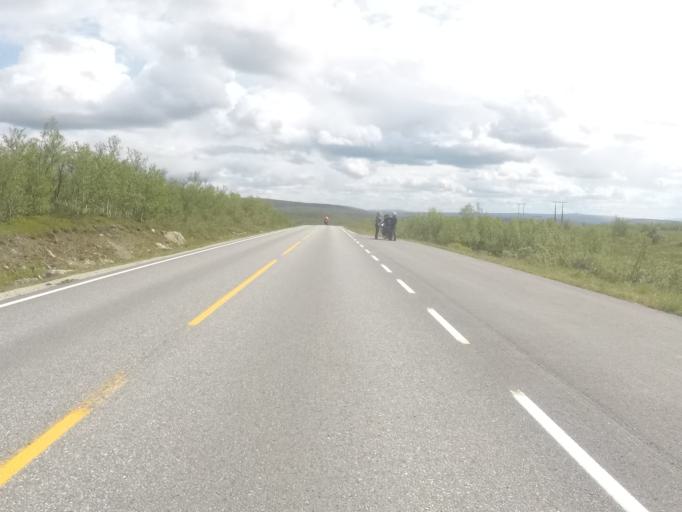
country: NO
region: Finnmark Fylke
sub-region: Karasjok
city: Karasjohka
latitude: 69.5555
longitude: 25.4013
